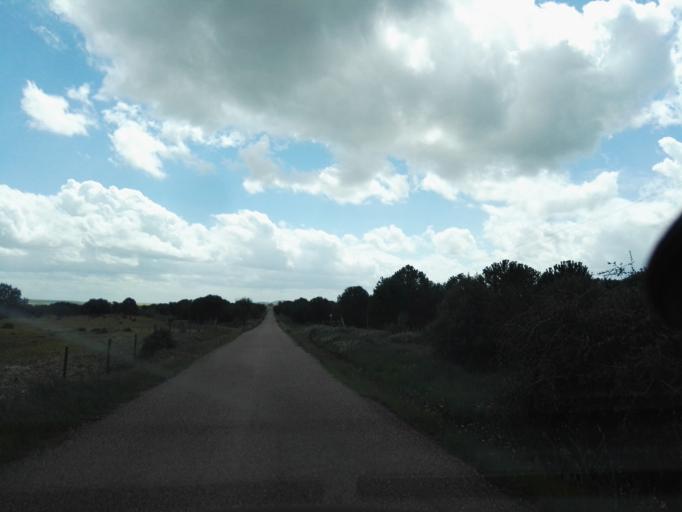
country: PT
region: Portalegre
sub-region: Elvas
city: Elvas
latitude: 38.9830
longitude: -7.1765
